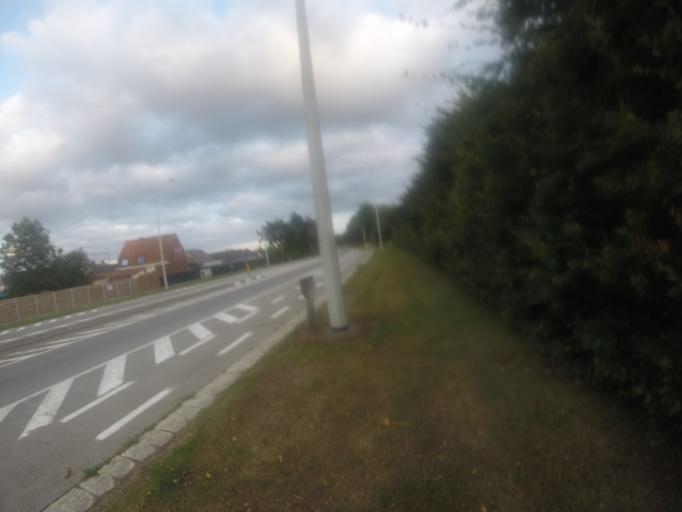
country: BE
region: Flanders
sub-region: Provincie West-Vlaanderen
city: Poperinge
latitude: 50.8508
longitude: 2.7080
